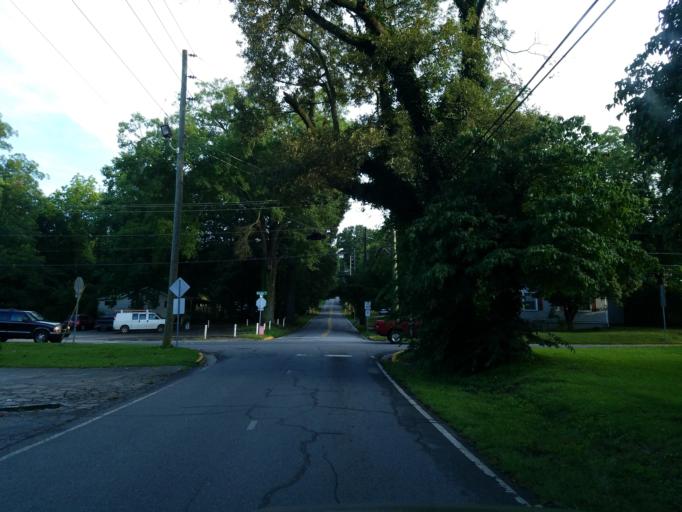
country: US
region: Georgia
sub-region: Bartow County
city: Cartersville
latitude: 34.1792
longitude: -84.7979
